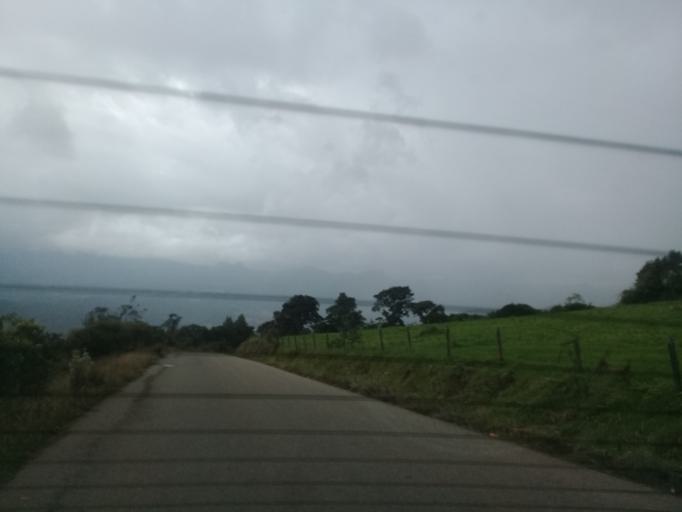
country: CO
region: Cundinamarca
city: Junin
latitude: 4.8426
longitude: -73.7474
